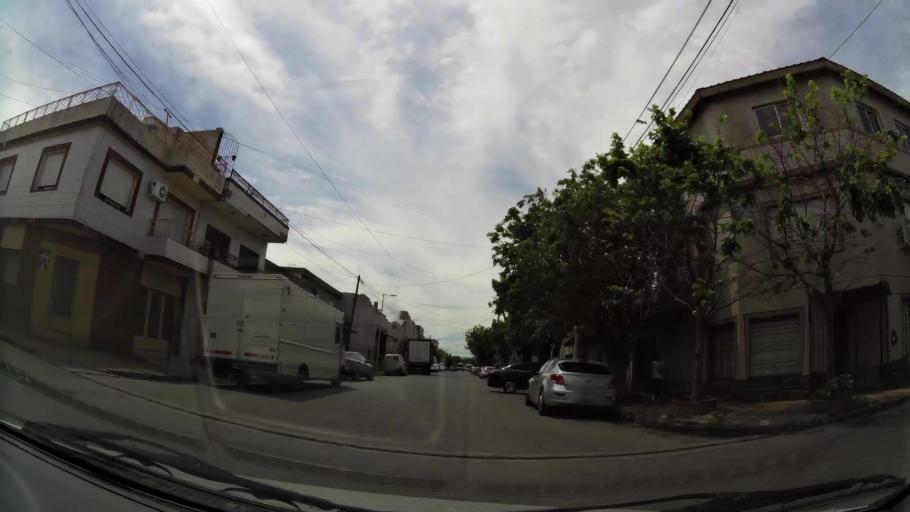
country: AR
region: Buenos Aires
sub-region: Partido de Avellaneda
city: Avellaneda
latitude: -34.6654
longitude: -58.3843
